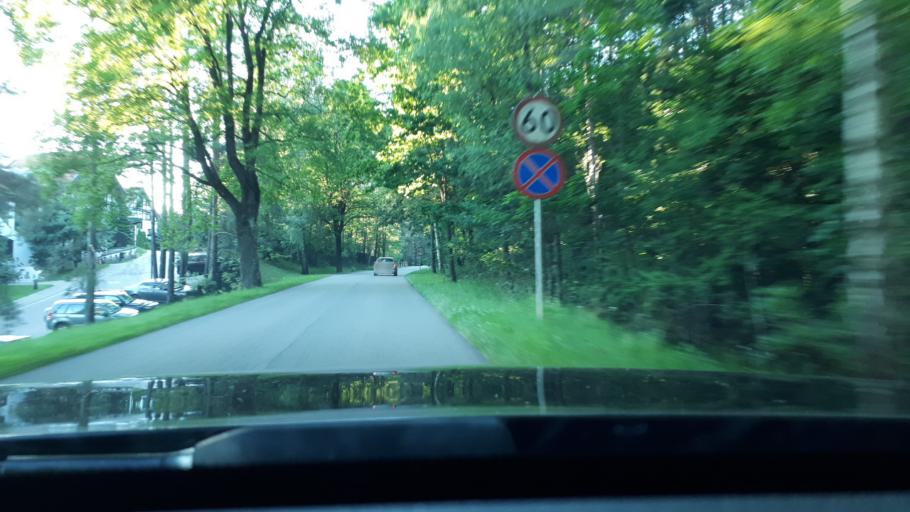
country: PL
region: Warmian-Masurian Voivodeship
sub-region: Powiat olsztynski
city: Stawiguda
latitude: 53.6126
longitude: 20.4173
